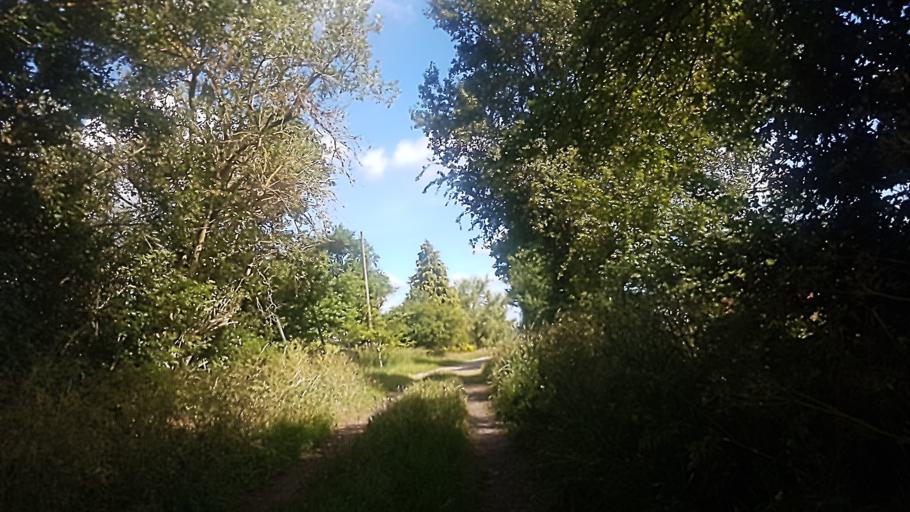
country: BE
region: Wallonia
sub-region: Province de Namur
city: Couvin
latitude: 50.0623
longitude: 4.5526
